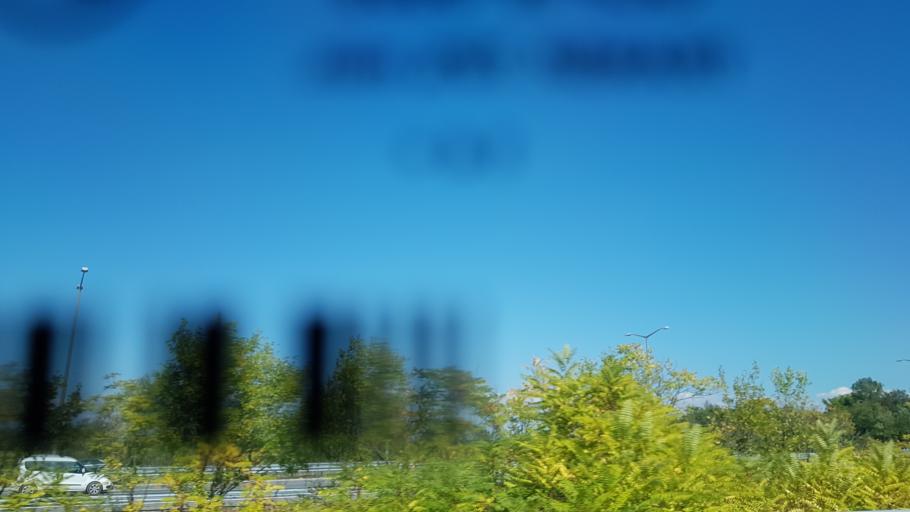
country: TR
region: Kirklareli
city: Luleburgaz
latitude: 41.4495
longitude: 27.3885
